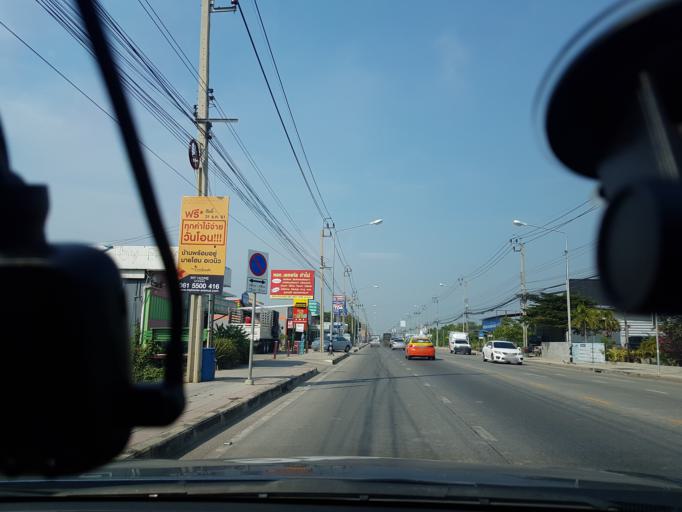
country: TH
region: Pathum Thani
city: Lam Luk Ka
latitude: 13.8881
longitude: 100.7221
